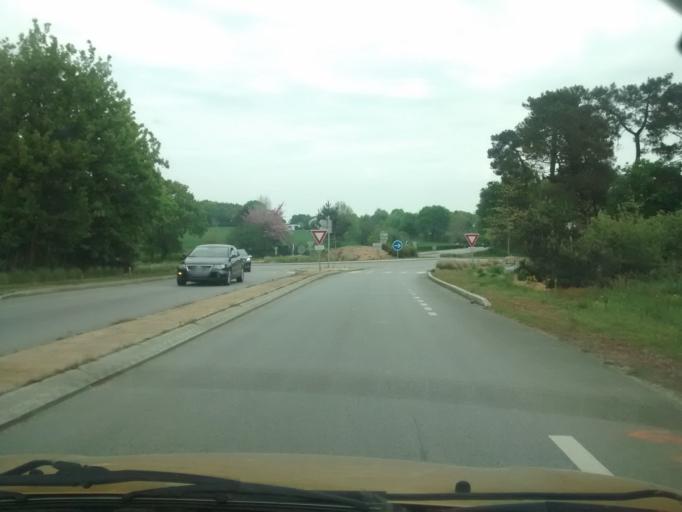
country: FR
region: Brittany
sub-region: Departement du Morbihan
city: Berric
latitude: 47.6145
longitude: -2.5402
